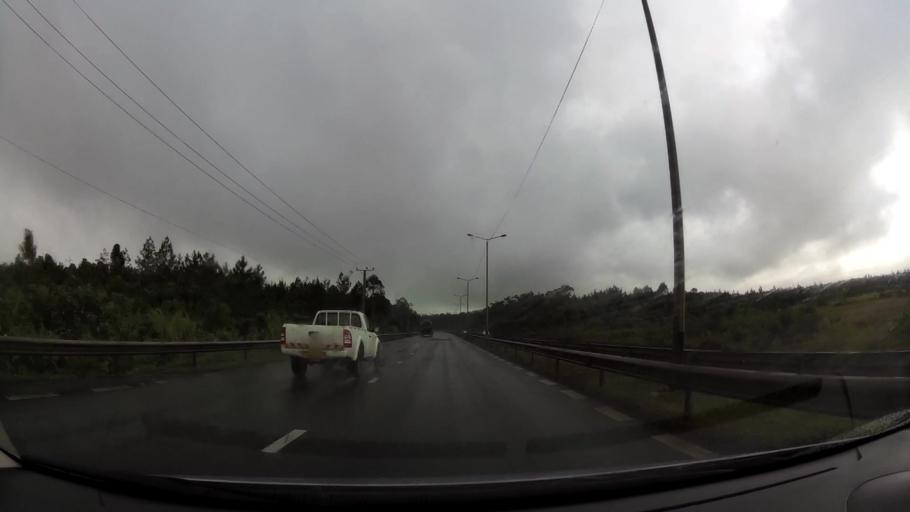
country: MU
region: Plaines Wilhems
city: Midlands
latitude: -20.3267
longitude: 57.5461
